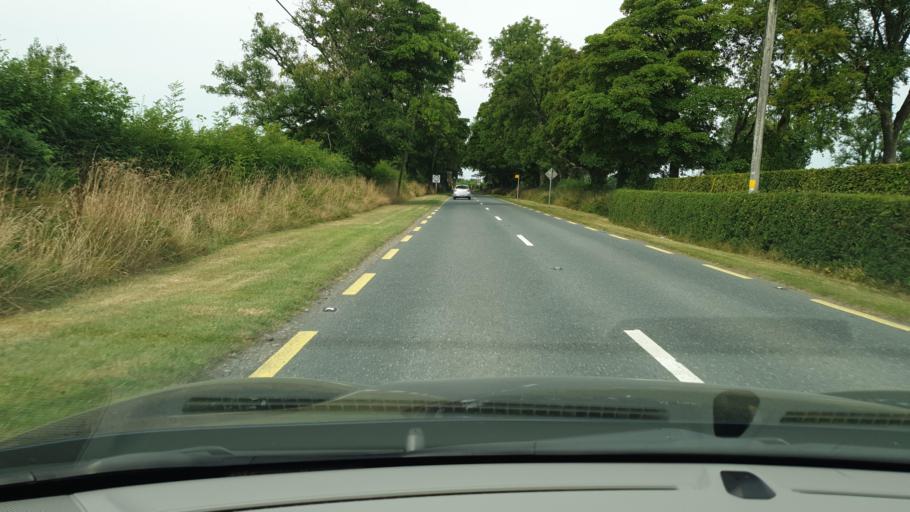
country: IE
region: Leinster
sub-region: An Mhi
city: Athboy
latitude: 53.6449
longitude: -6.8536
